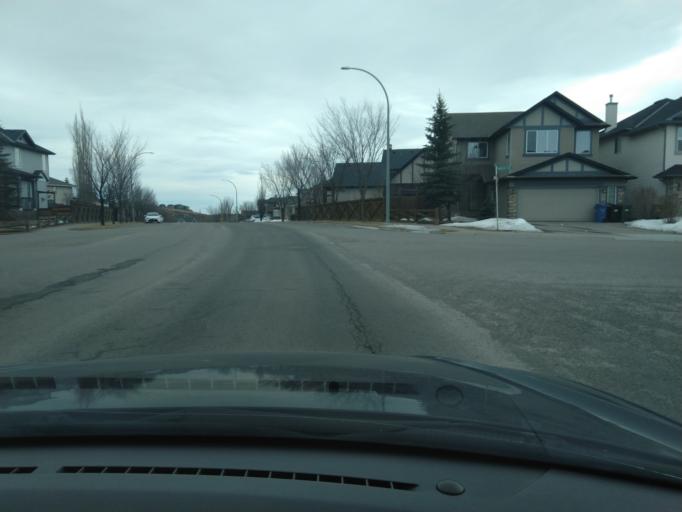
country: CA
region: Alberta
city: Calgary
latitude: 51.1621
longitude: -114.1025
